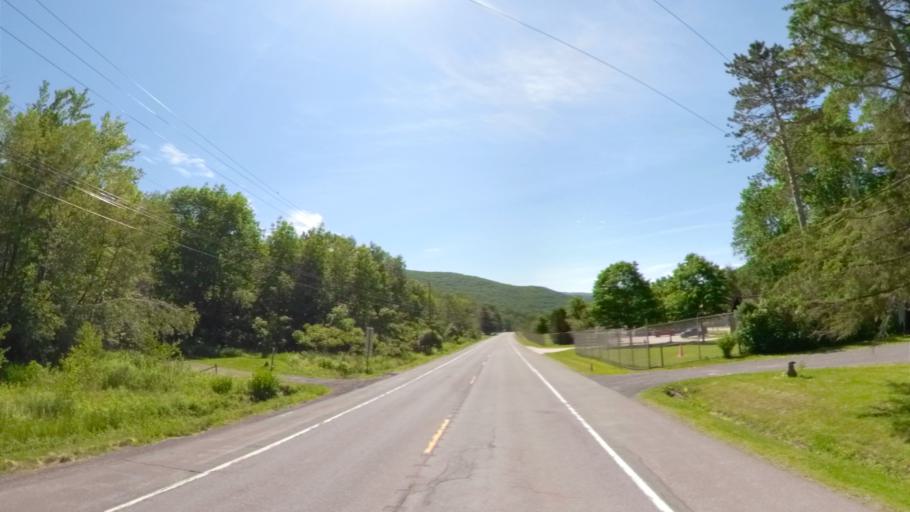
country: US
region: New York
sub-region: Ulster County
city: Shokan
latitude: 42.1238
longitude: -74.4650
